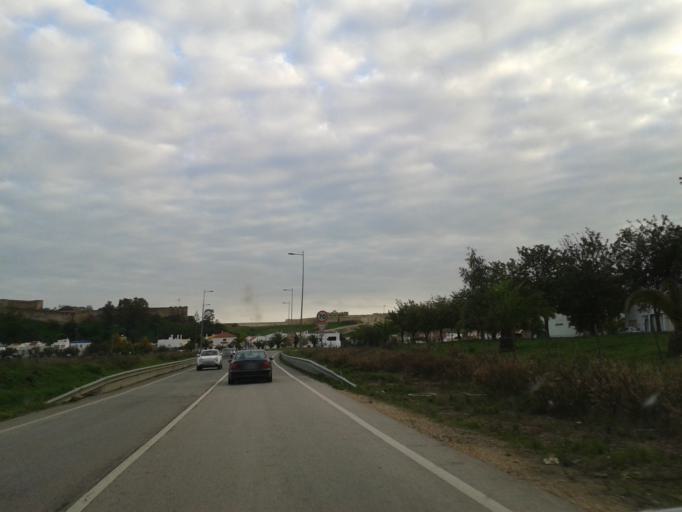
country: PT
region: Faro
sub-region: Castro Marim
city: Castro Marim
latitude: 37.2230
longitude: -7.4449
